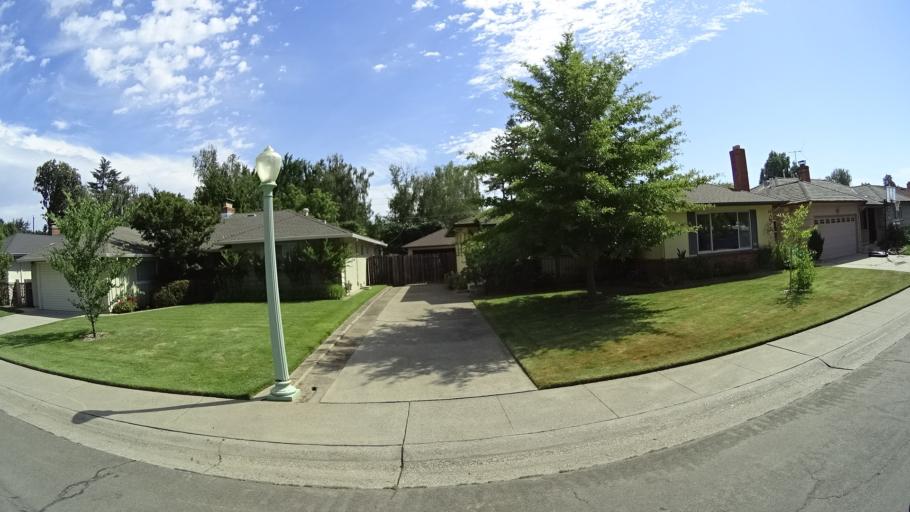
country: US
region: California
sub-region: Sacramento County
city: Arden-Arcade
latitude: 38.5768
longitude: -121.4265
